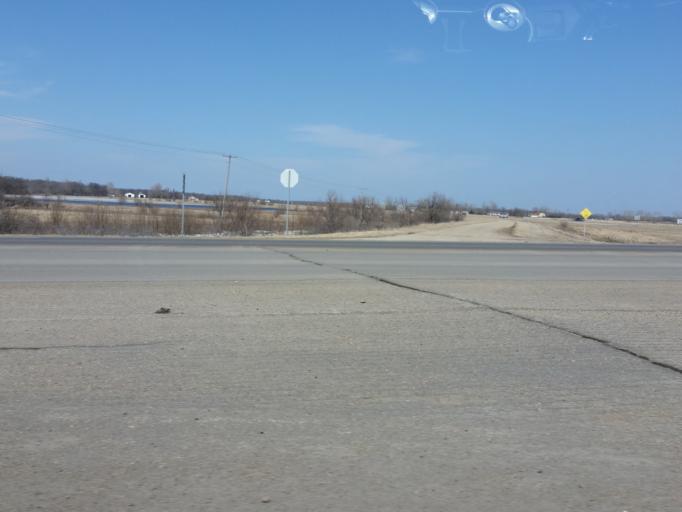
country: US
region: North Dakota
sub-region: Grand Forks County
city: Grand Forks
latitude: 48.0776
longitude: -97.1721
